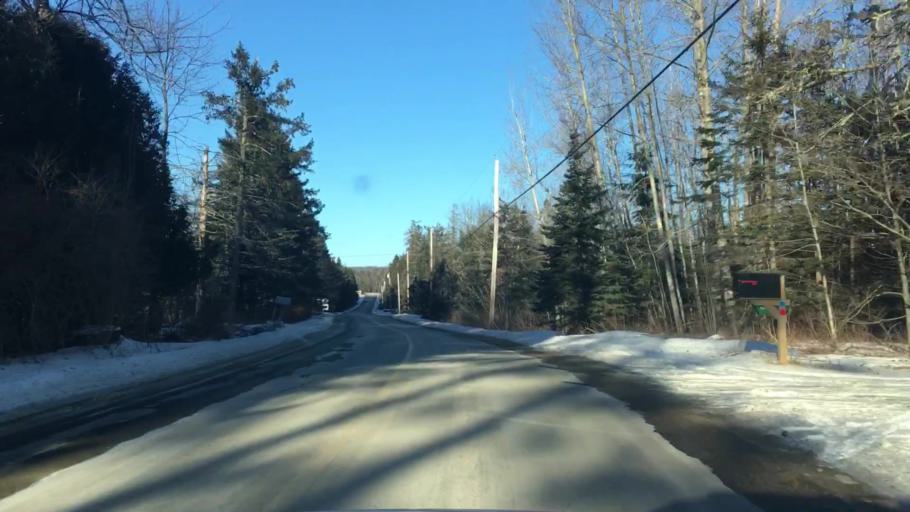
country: US
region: Maine
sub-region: Hancock County
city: Penobscot
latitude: 44.3987
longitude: -68.6977
